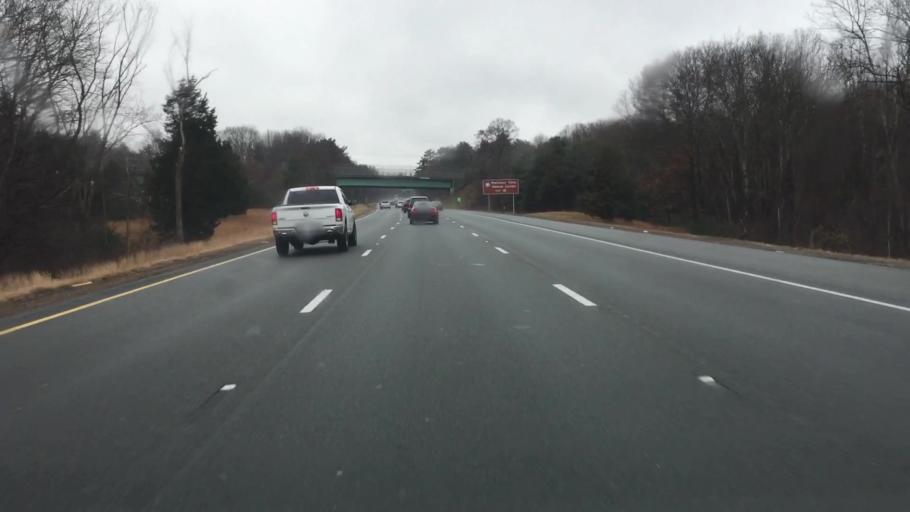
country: US
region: Massachusetts
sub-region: Norfolk County
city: Bellingham
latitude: 42.1254
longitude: -71.4726
